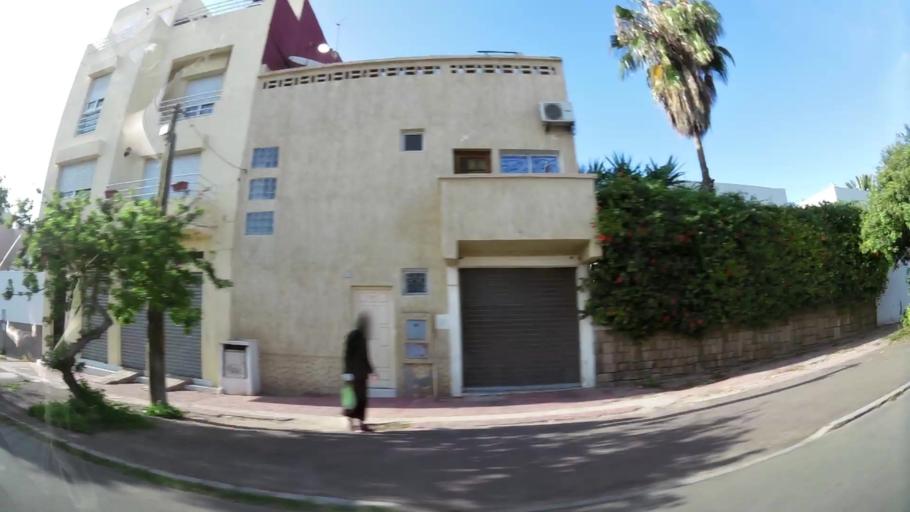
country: MA
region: Souss-Massa-Draa
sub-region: Agadir-Ida-ou-Tnan
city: Agadir
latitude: 30.4272
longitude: -9.5899
